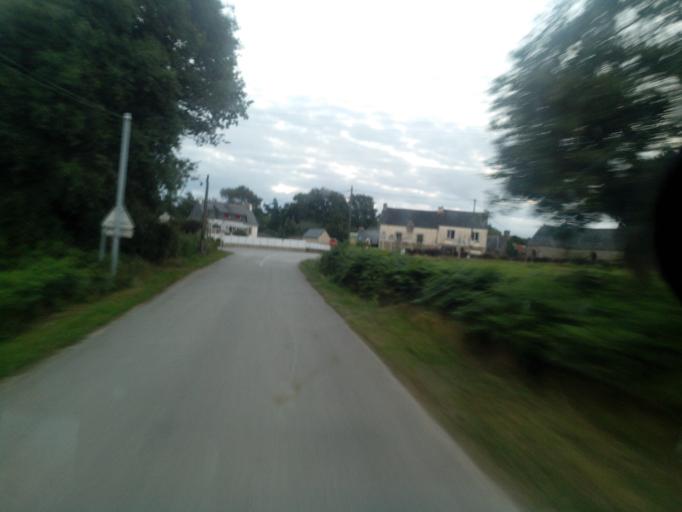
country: FR
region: Brittany
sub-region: Departement du Morbihan
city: Plumelec
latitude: 47.8773
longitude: -2.6051
